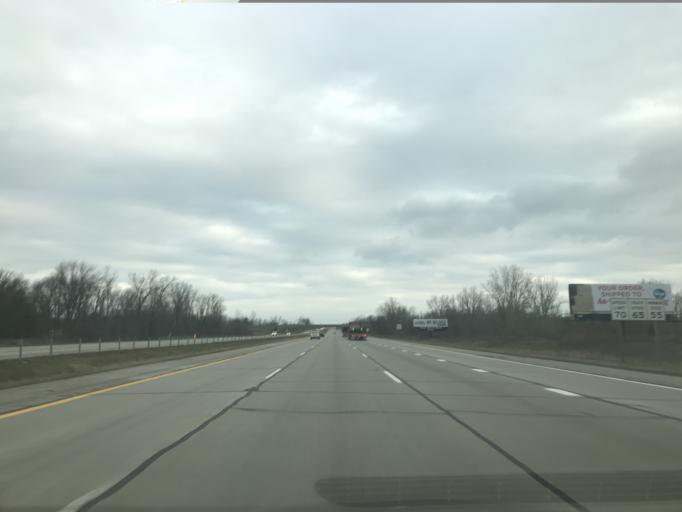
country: US
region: Michigan
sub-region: Eaton County
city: Waverly
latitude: 42.7075
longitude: -84.6693
